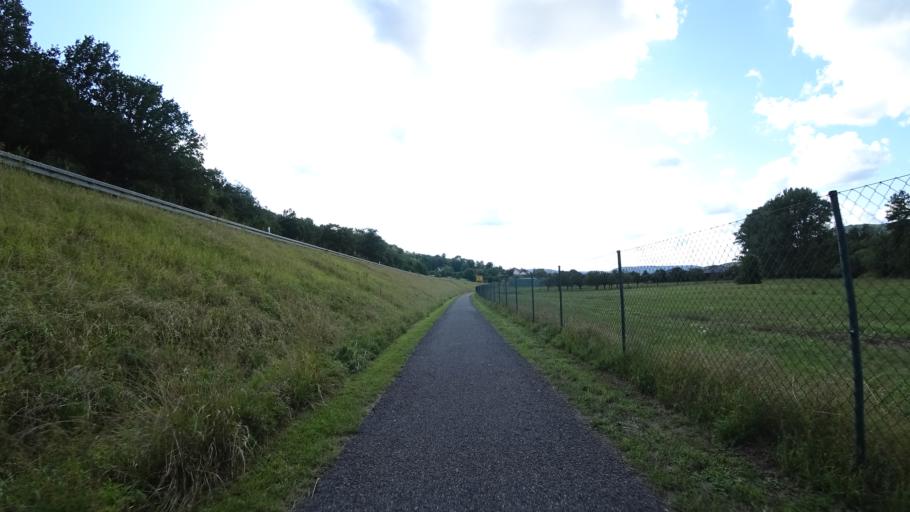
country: DE
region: Bavaria
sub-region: Regierungsbezirk Unterfranken
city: Miltenberg
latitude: 49.7045
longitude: 9.2874
